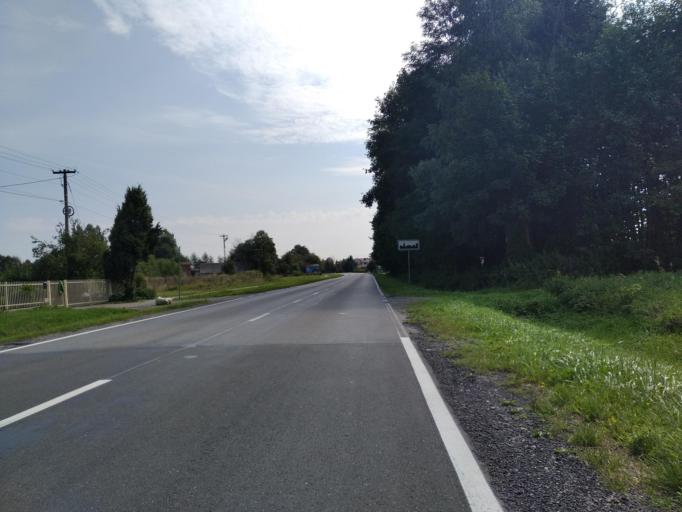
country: PL
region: Subcarpathian Voivodeship
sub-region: Powiat mielecki
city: Przeclaw
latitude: 50.1647
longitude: 21.5123
